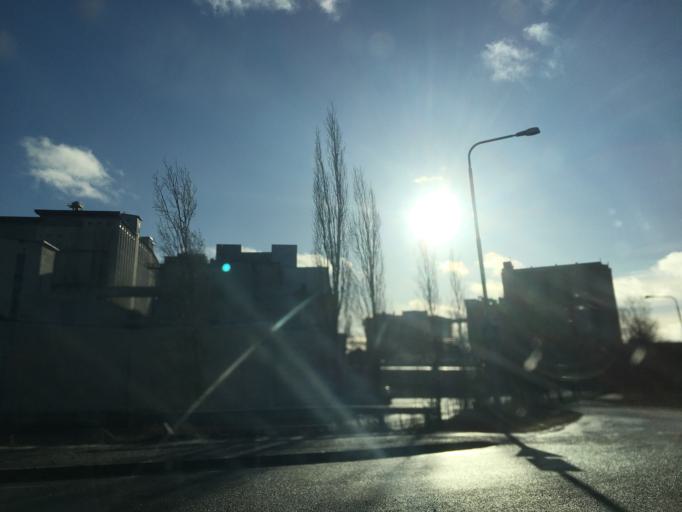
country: FI
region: Varsinais-Suomi
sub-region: Turku
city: Raisio
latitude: 60.4872
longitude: 22.1320
